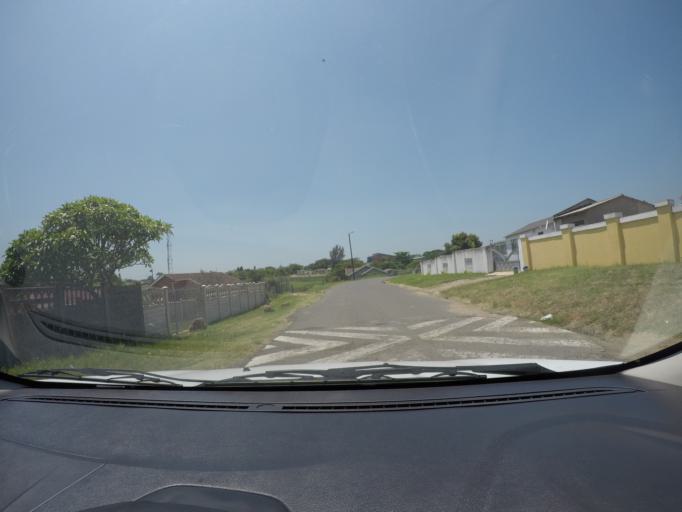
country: ZA
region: KwaZulu-Natal
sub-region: uThungulu District Municipality
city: eSikhawini
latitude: -28.8756
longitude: 31.9123
